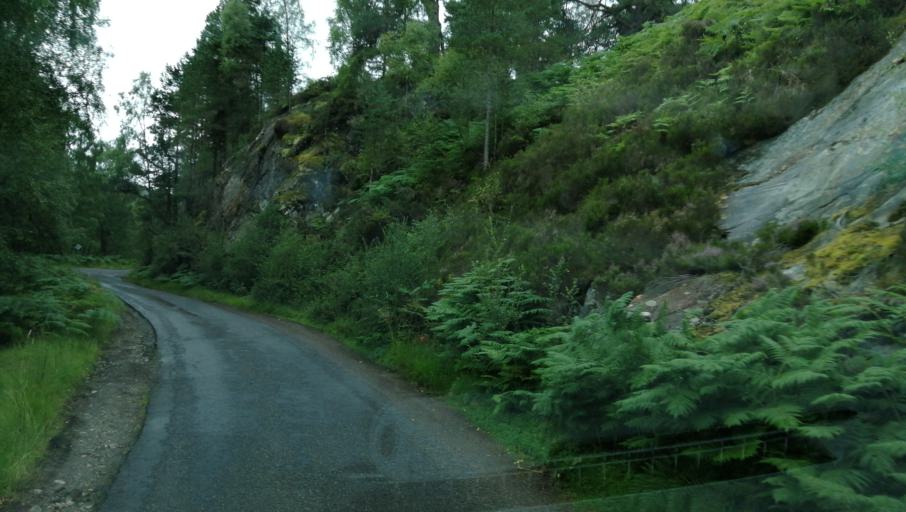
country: GB
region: Scotland
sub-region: Highland
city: Spean Bridge
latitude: 57.3079
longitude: -4.8672
